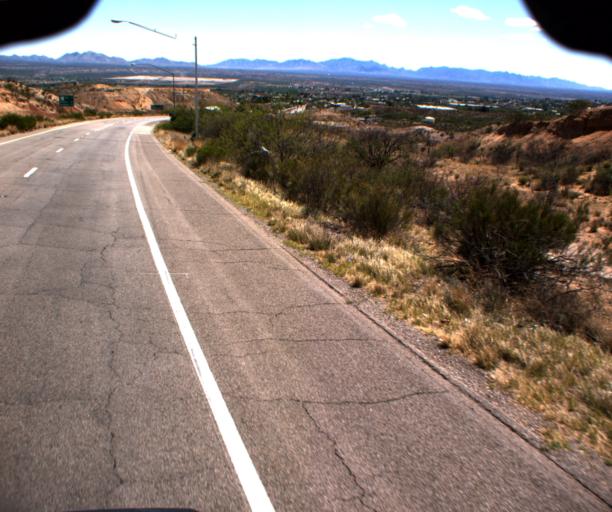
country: US
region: Arizona
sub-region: Cochise County
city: Whetstone
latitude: 31.9710
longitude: -110.3272
